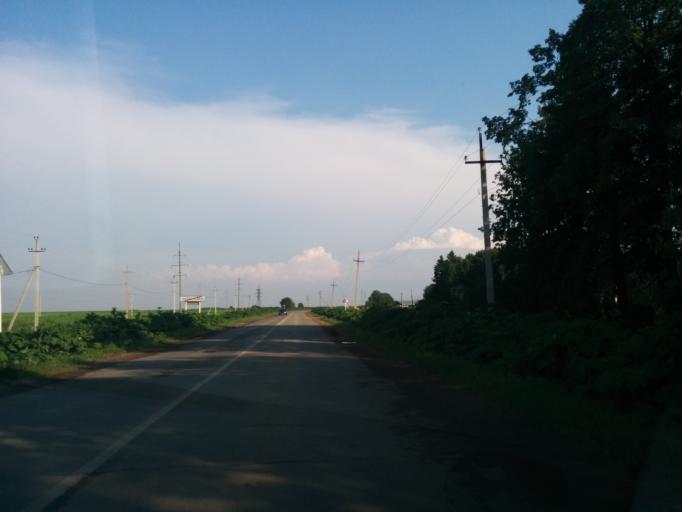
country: RU
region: Perm
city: Polazna
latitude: 58.2249
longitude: 56.2949
